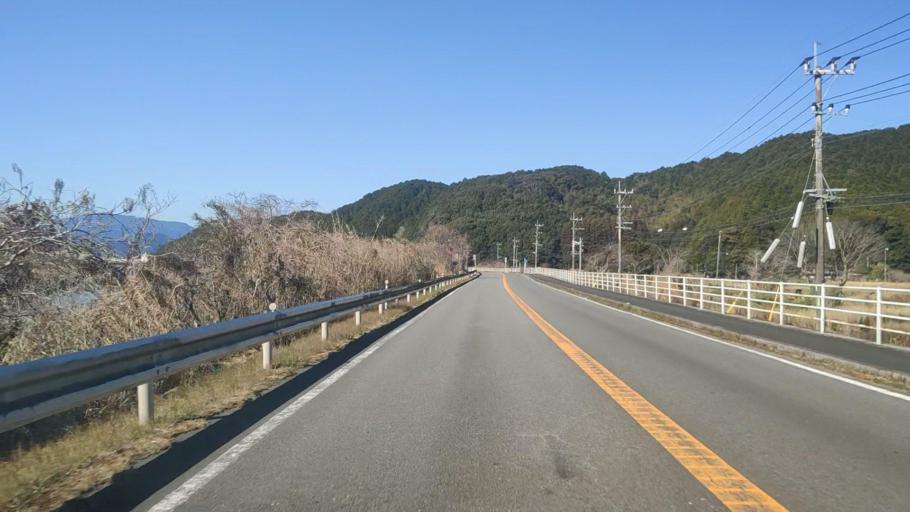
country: JP
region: Oita
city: Saiki
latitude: 32.9382
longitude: 131.9156
